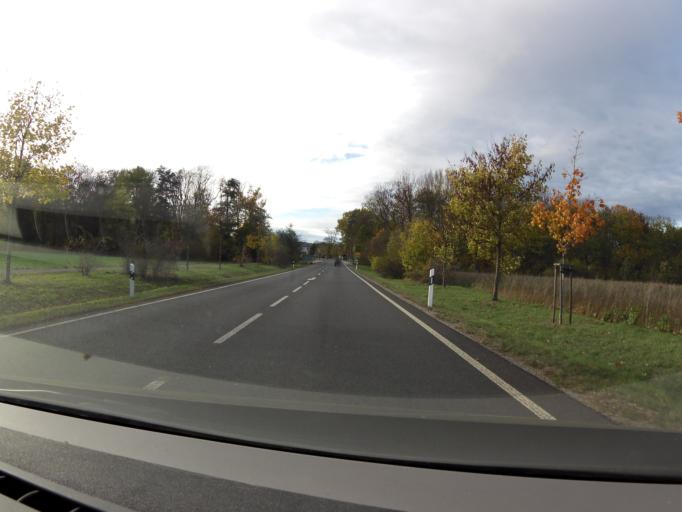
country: DE
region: Thuringia
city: Luisenthal
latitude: 50.8126
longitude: 10.7359
